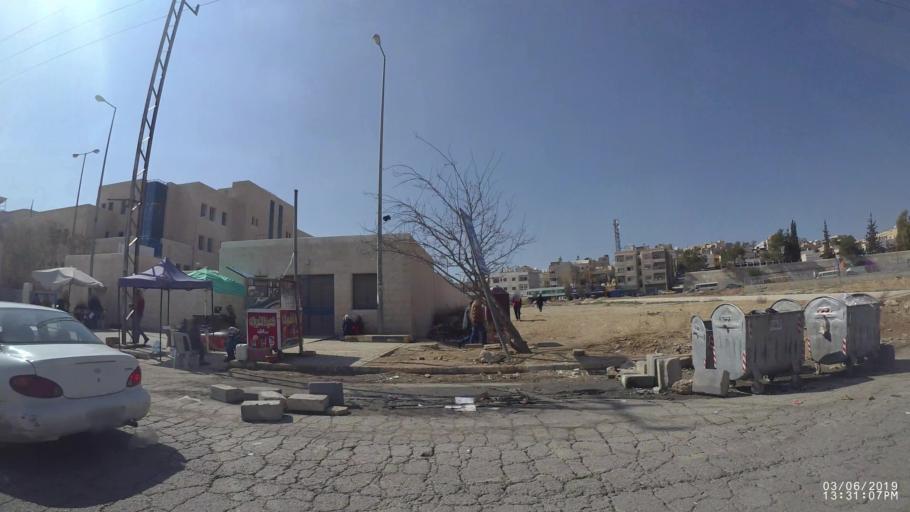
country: JO
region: Zarqa
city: Zarqa
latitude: 32.0767
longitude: 36.1040
